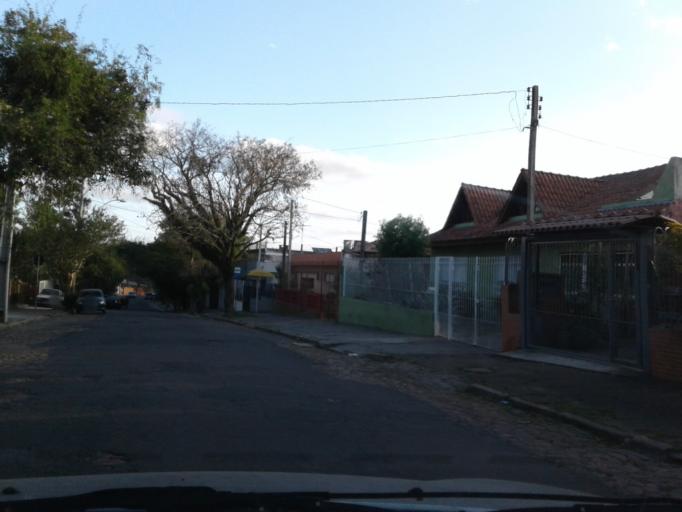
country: BR
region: Rio Grande do Sul
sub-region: Porto Alegre
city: Porto Alegre
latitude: -30.0458
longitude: -51.1497
